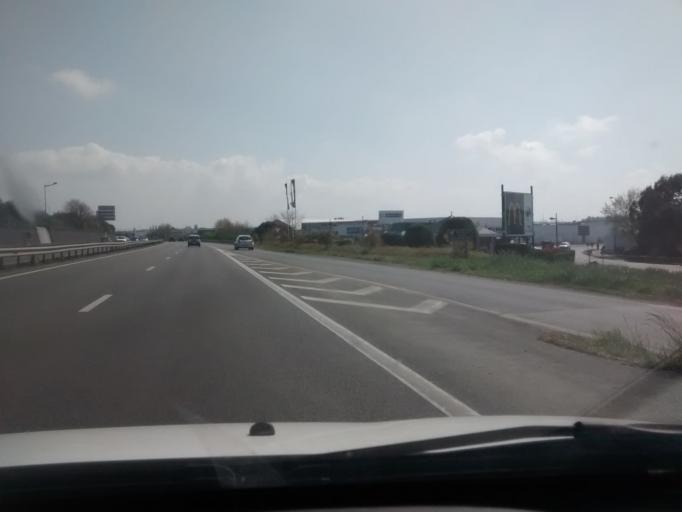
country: FR
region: Brittany
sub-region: Departement des Cotes-d'Armor
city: Langueux
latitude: 48.4956
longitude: -2.7241
